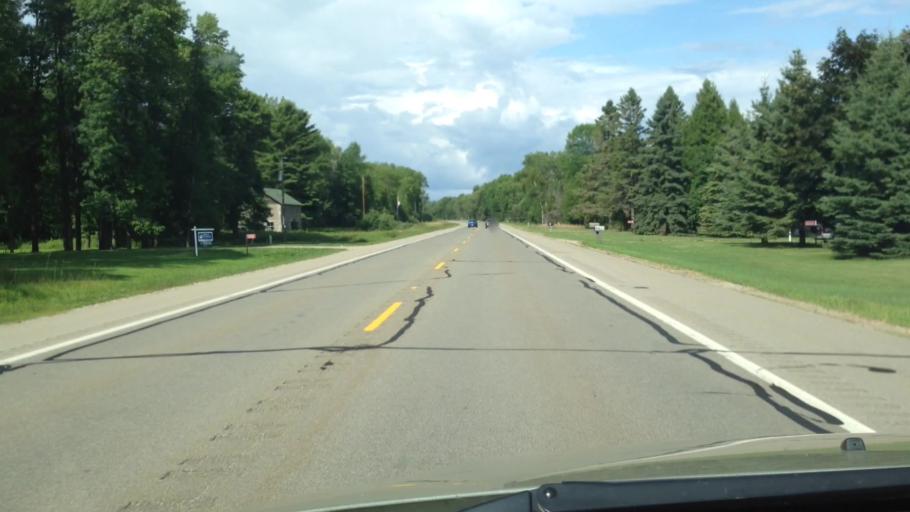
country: US
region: Michigan
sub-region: Menominee County
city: Menominee
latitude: 45.2578
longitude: -87.4798
